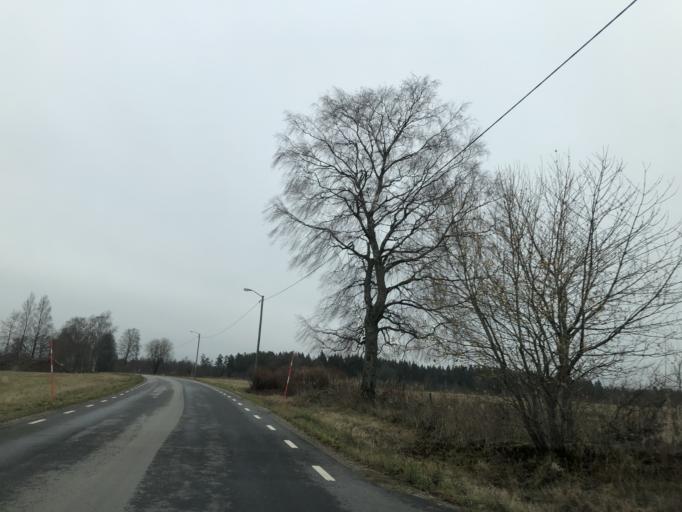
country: SE
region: Vaestra Goetaland
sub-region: Ulricehamns Kommun
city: Ulricehamn
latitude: 57.6819
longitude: 13.4727
